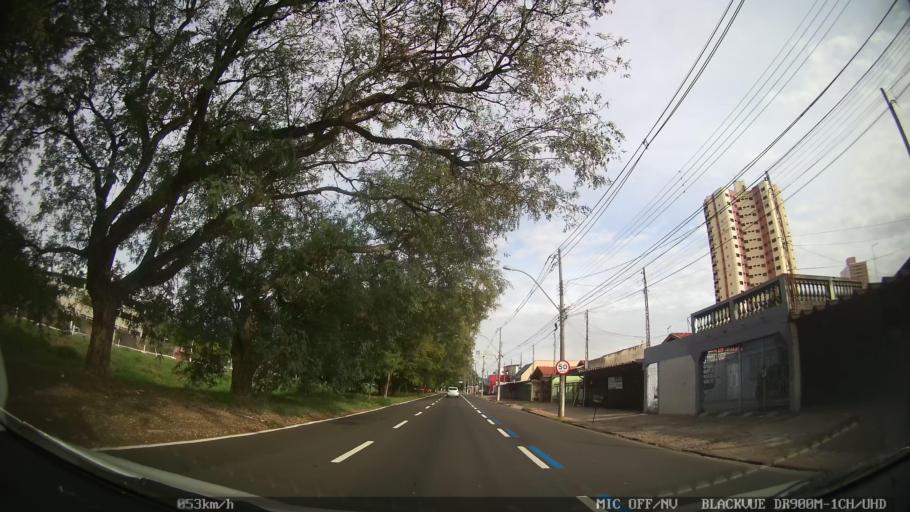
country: BR
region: Sao Paulo
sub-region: Piracicaba
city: Piracicaba
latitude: -22.7286
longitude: -47.6275
